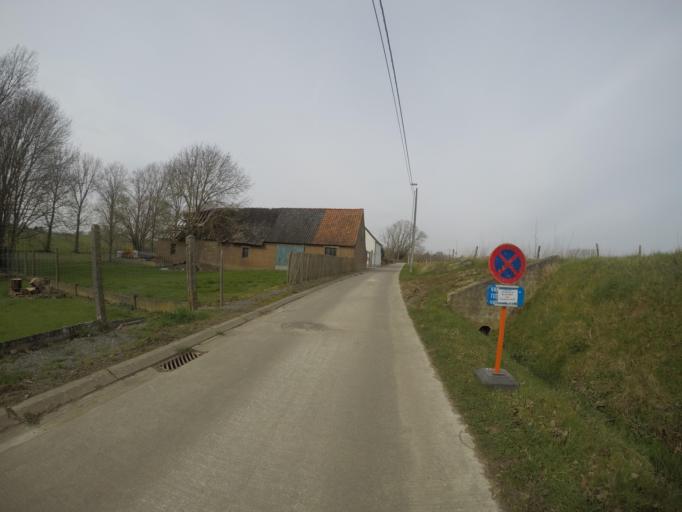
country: BE
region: Flanders
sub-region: Provincie Oost-Vlaanderen
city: Sint-Maria-Lierde
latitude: 50.8255
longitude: 3.8551
